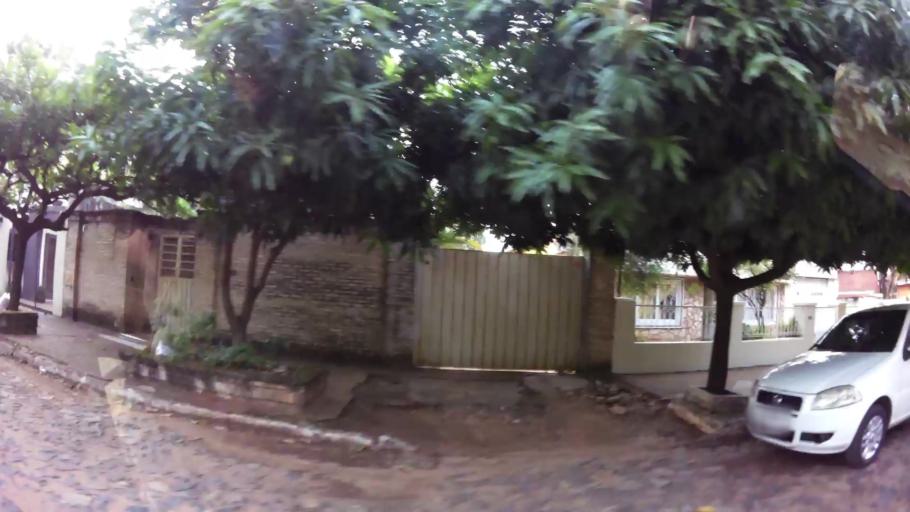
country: PY
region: Central
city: Lambare
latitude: -25.3180
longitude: -57.5773
